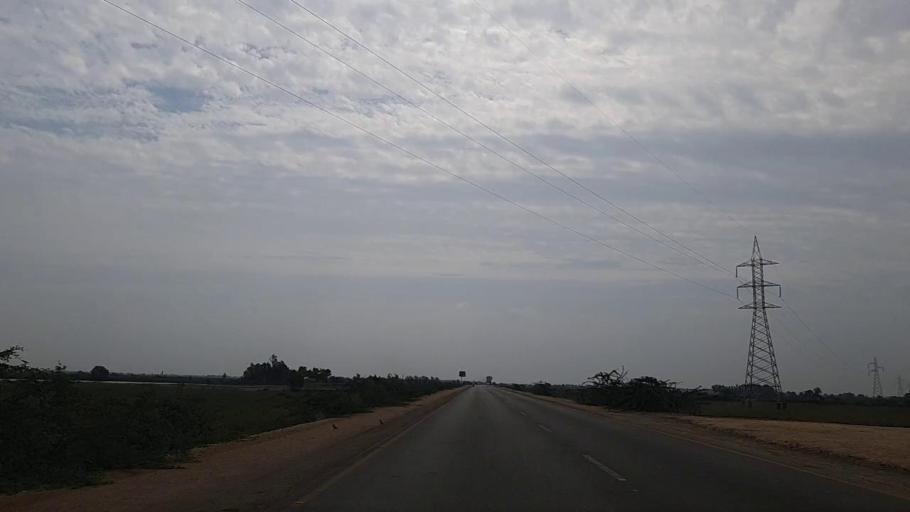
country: PK
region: Sindh
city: Daro Mehar
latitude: 24.6124
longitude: 68.0903
